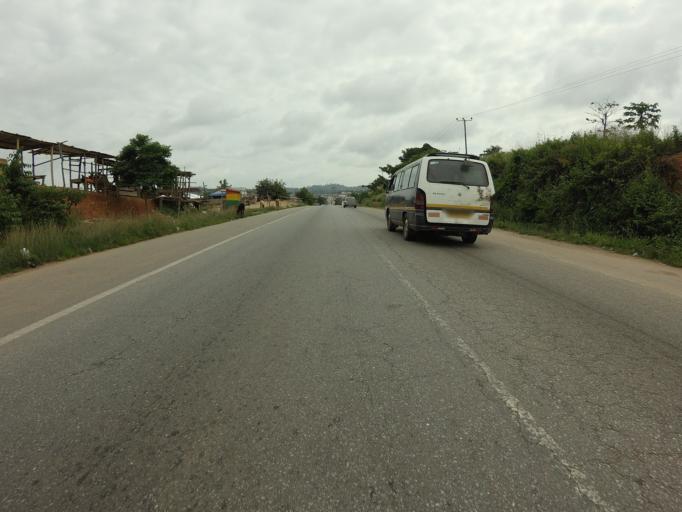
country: GH
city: Bechem
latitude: 7.1247
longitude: -1.7340
